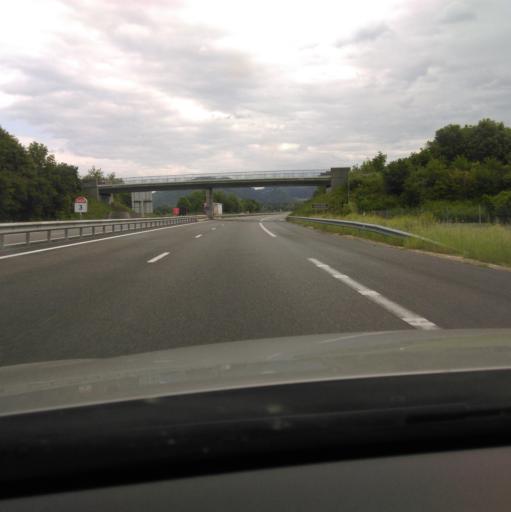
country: FR
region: Rhone-Alpes
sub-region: Departement de l'Ain
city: Saint-Martin-du-Frene
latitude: 46.1553
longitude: 5.5484
